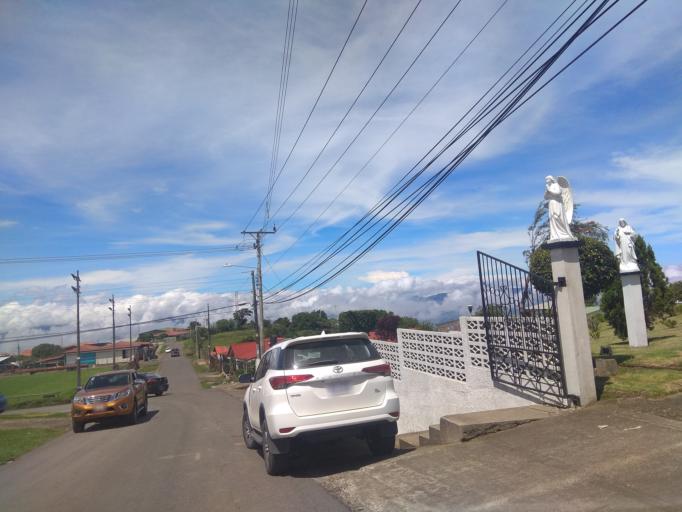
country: CR
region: Cartago
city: Cot
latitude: 9.9159
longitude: -83.8960
